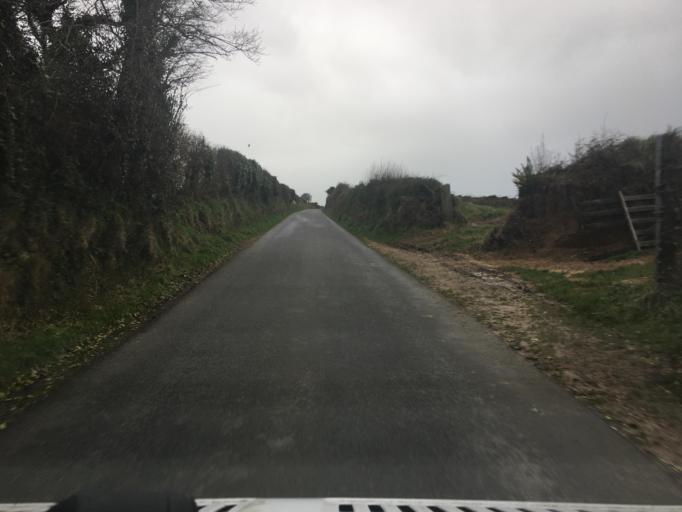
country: FR
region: Lower Normandy
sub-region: Departement de la Manche
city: Beaumont-Hague
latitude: 49.6827
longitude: -1.8577
